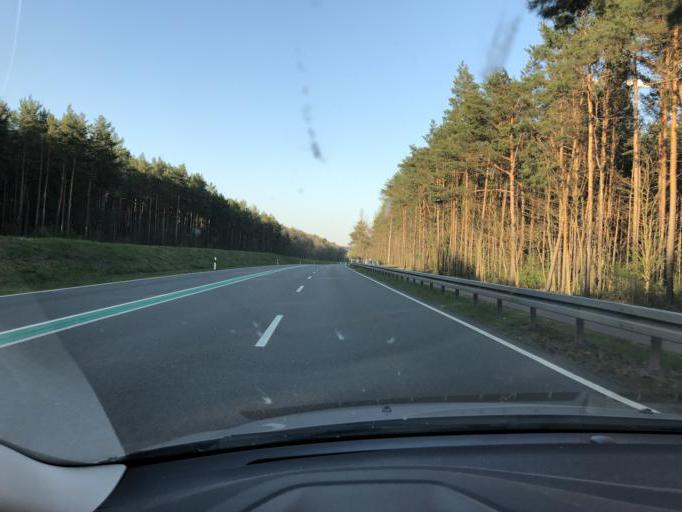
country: DE
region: Brandenburg
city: Schwarzbach
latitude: 51.4822
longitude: 13.9231
